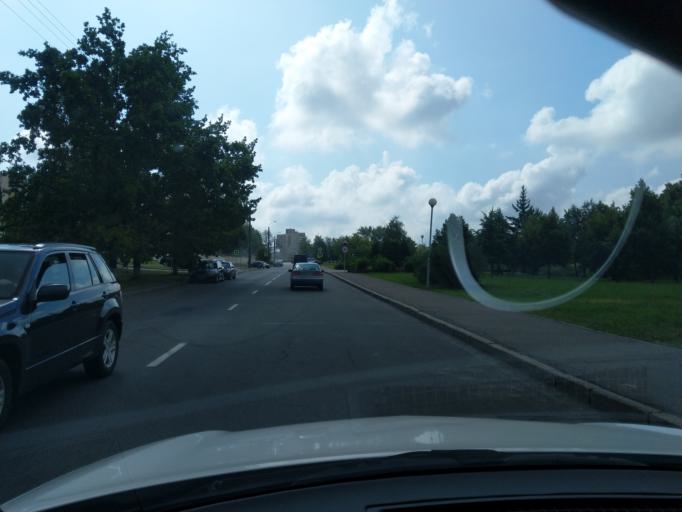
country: BY
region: Minsk
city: Minsk
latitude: 53.8943
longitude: 27.5829
